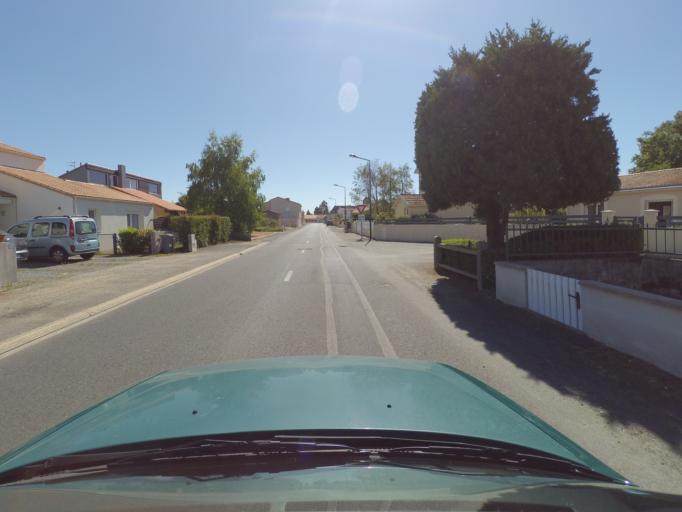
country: FR
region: Pays de la Loire
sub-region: Departement de la Loire-Atlantique
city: Le Bignon
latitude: 47.1003
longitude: -1.4928
